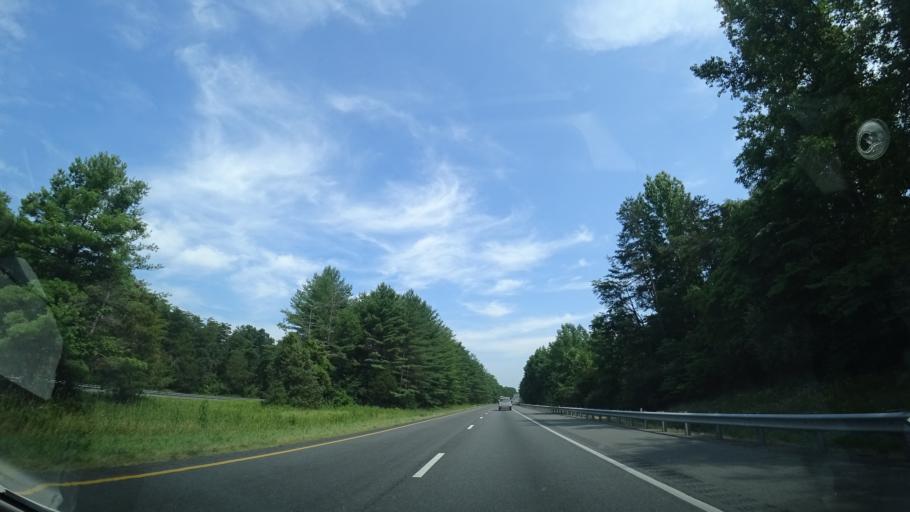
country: US
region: Virginia
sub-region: Louisa County
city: Louisa
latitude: 37.9285
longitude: -78.0877
